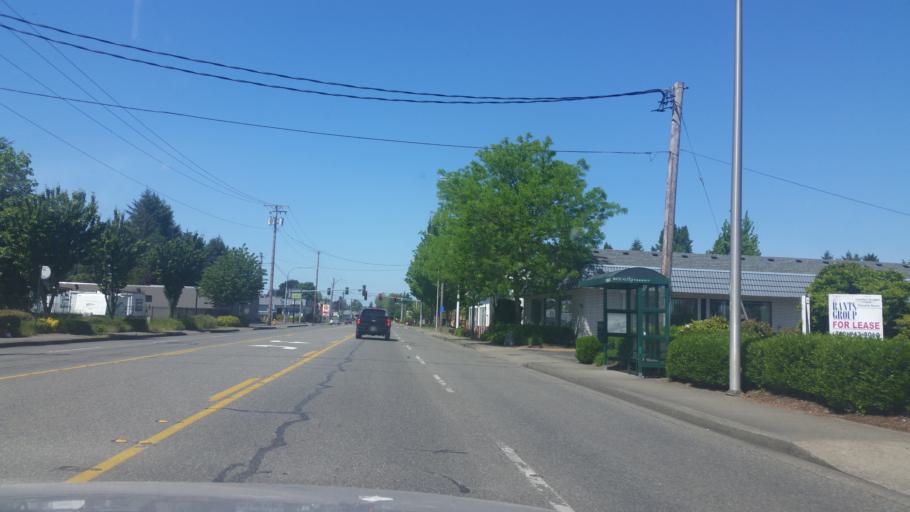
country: US
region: Washington
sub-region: Thurston County
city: Tumwater
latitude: 46.9995
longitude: -122.9086
